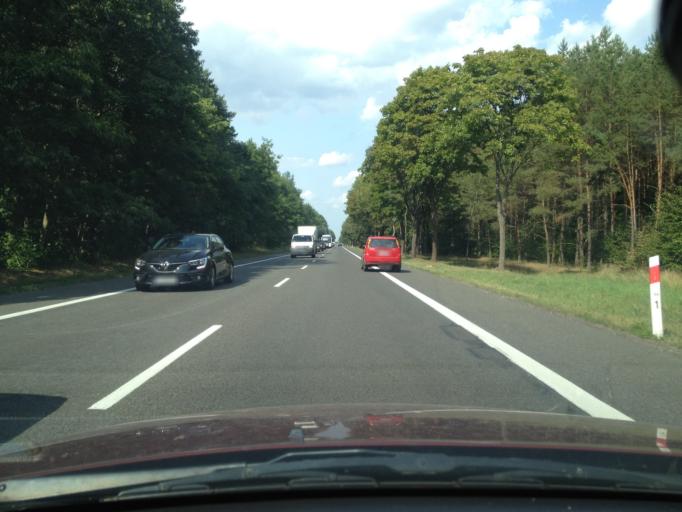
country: PL
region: West Pomeranian Voivodeship
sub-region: Powiat goleniowski
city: Przybiernow
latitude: 53.7793
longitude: 14.7776
